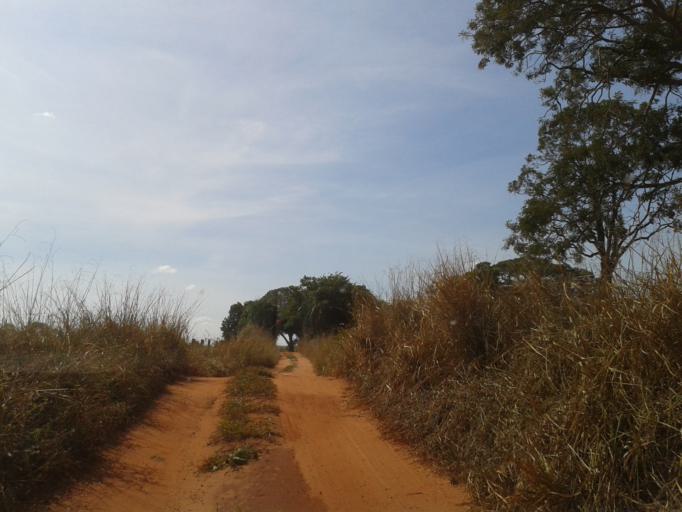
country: BR
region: Minas Gerais
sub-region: Campina Verde
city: Campina Verde
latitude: -19.5217
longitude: -49.5933
